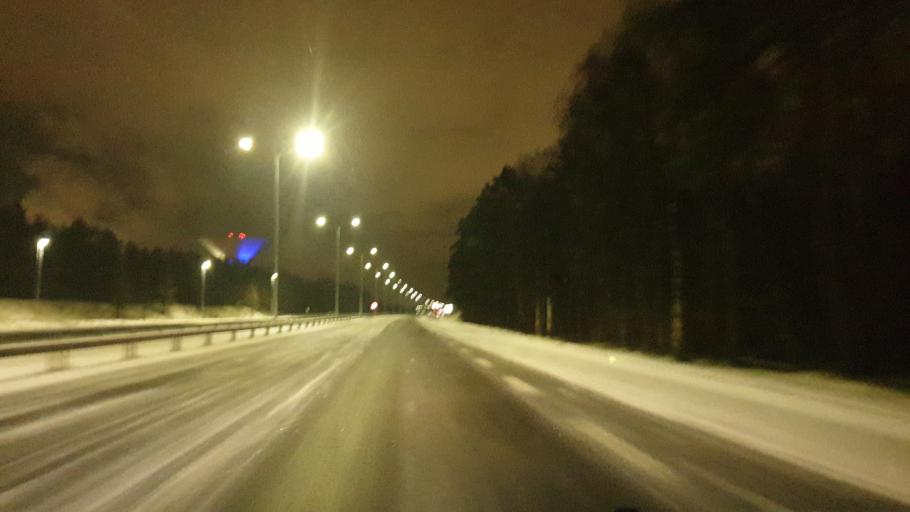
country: FI
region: Northern Ostrobothnia
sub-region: Oulu
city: Oulu
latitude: 65.0394
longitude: 25.4765
